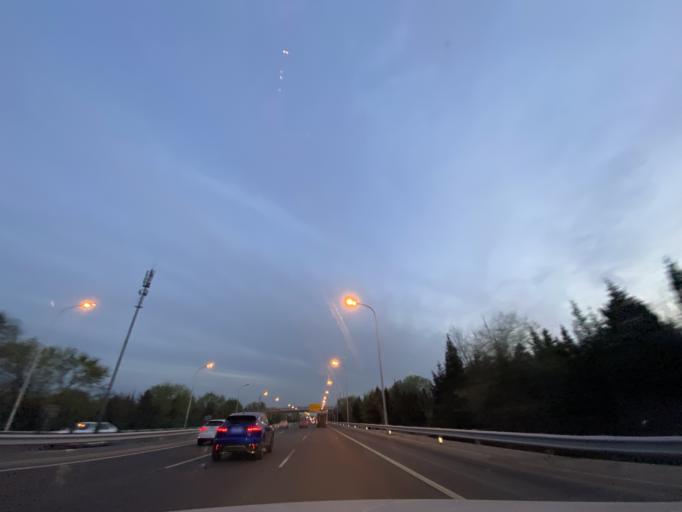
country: CN
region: Beijing
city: Xiangshan
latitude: 39.9656
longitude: 116.2124
